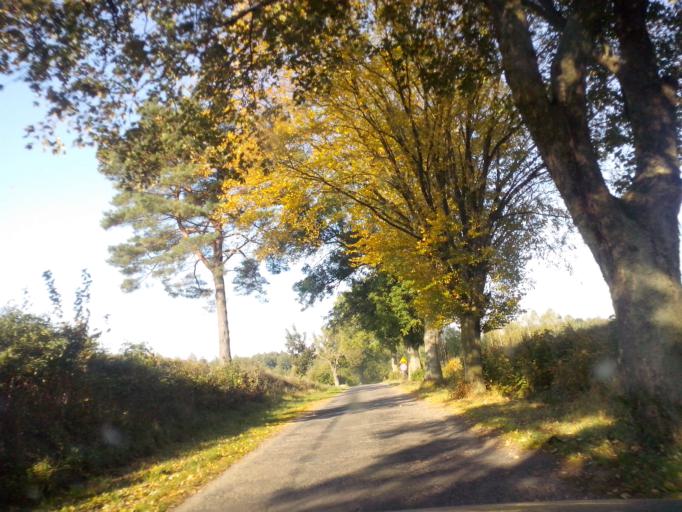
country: PL
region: Kujawsko-Pomorskie
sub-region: Powiat brodnicki
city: Gorzno
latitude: 53.2613
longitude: 19.6838
